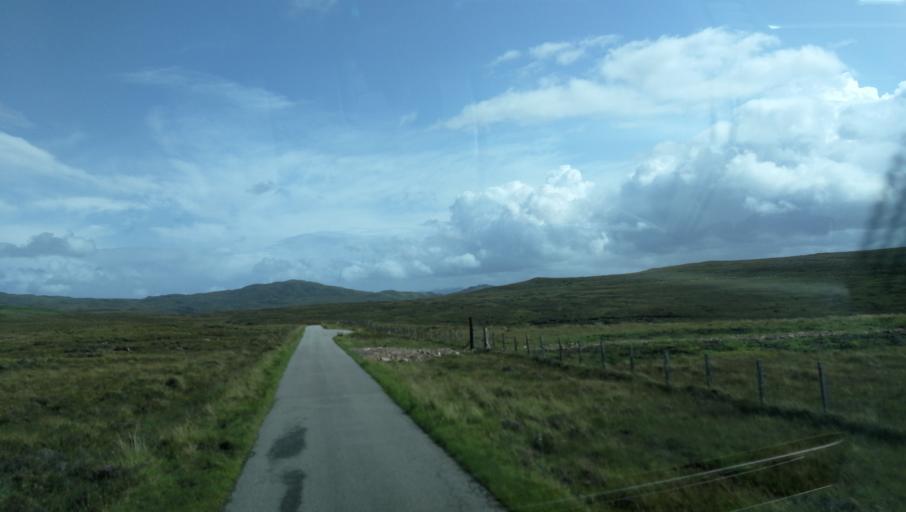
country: GB
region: Scotland
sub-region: Highland
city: Portree
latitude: 57.7490
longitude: -5.7658
